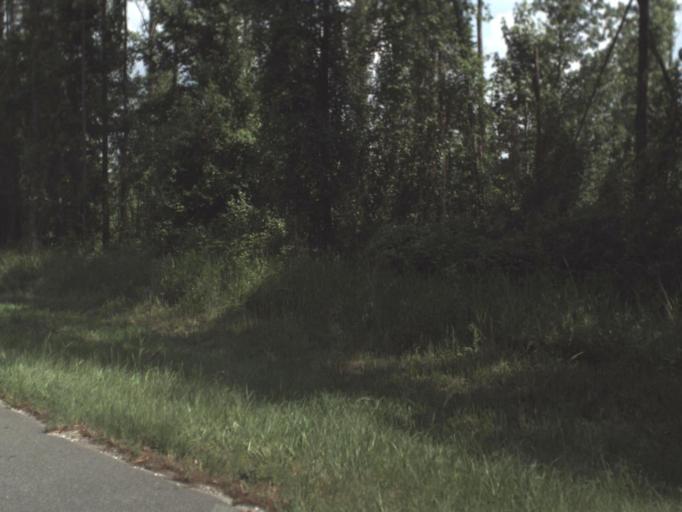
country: US
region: Florida
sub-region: Putnam County
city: Interlachen
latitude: 29.7014
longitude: -81.7713
